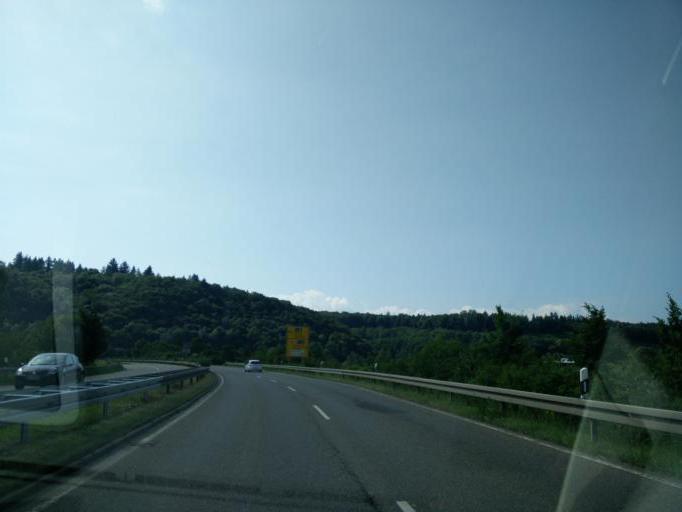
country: DE
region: Baden-Wuerttemberg
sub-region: Tuebingen Region
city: Kusterdingen
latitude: 48.5187
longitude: 9.0861
